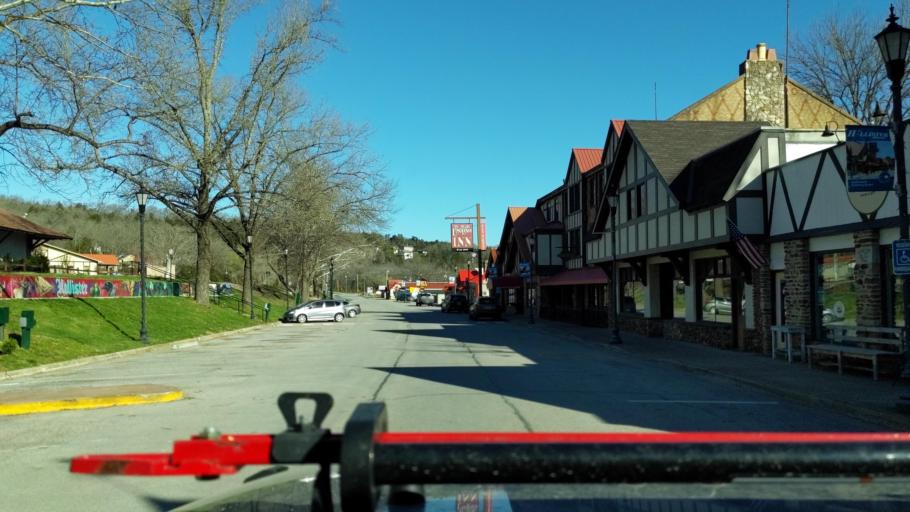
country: US
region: Missouri
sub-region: Taney County
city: Hollister
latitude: 36.6234
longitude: -93.2163
